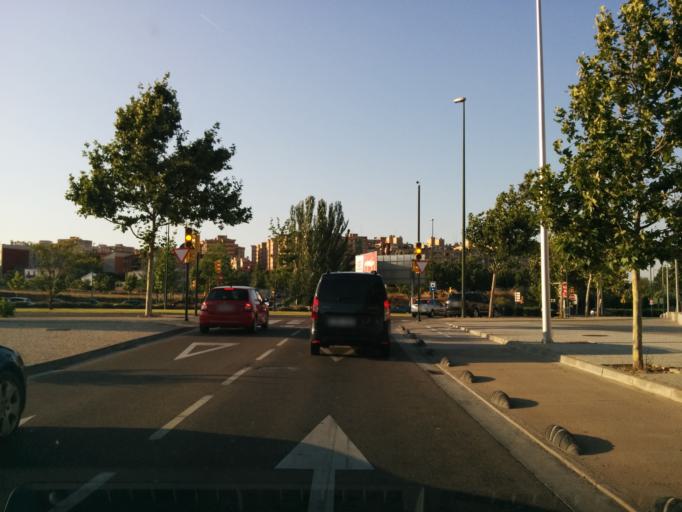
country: ES
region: Aragon
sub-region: Provincia de Zaragoza
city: Zaragoza
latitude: 41.6201
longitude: -0.8761
